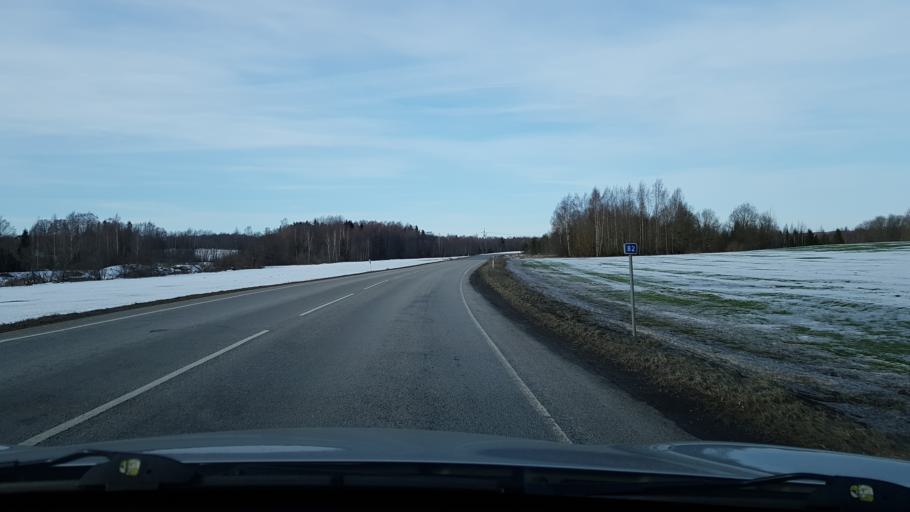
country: EE
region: Viljandimaa
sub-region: Viljandi linn
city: Viljandi
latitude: 58.3407
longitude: 25.4690
